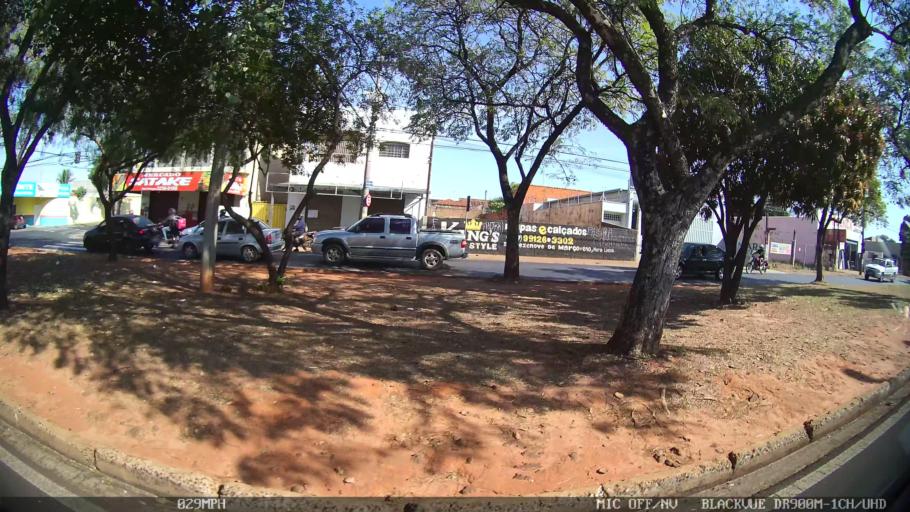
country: BR
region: Sao Paulo
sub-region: Sao Jose Do Rio Preto
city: Sao Jose do Rio Preto
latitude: -20.7740
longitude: -49.3856
